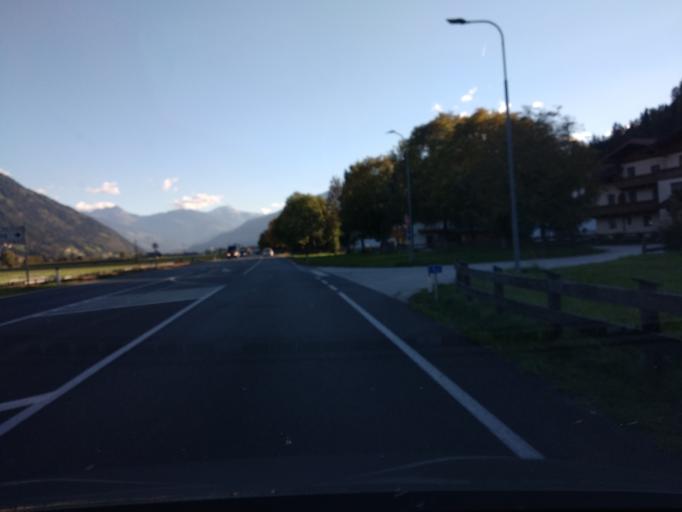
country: AT
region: Tyrol
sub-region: Politischer Bezirk Schwaz
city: Fugenberg
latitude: 47.3624
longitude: 11.8518
